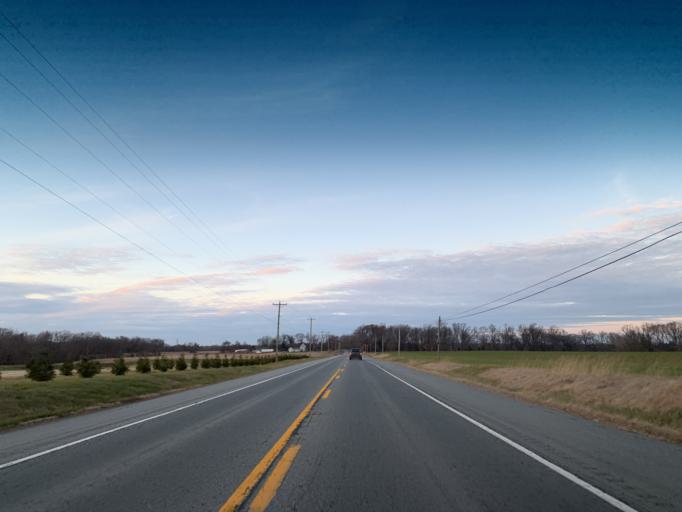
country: US
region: Delaware
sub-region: New Castle County
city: Middletown
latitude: 39.4484
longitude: -75.8692
